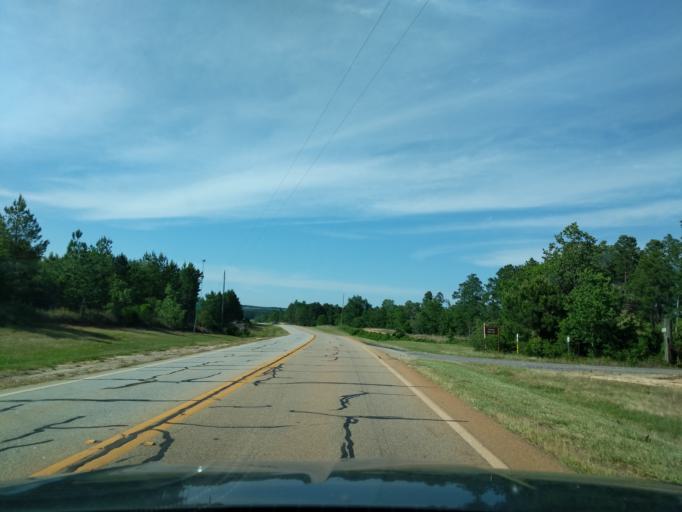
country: US
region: Georgia
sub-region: Jefferson County
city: Wrens
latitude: 33.2966
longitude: -82.3771
